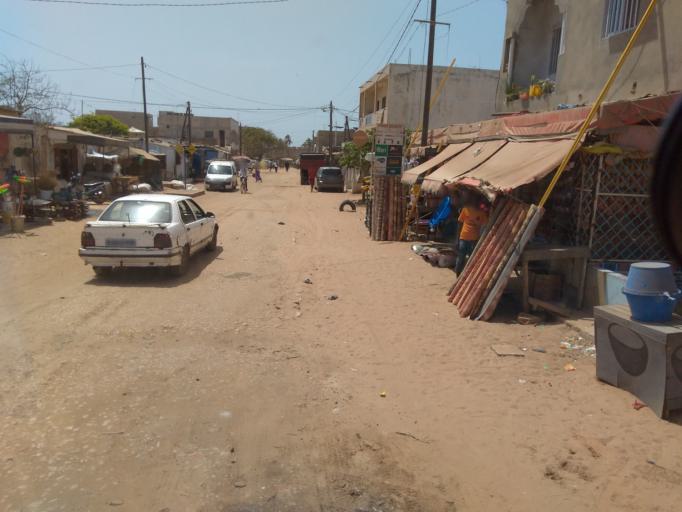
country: SN
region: Dakar
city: Pikine
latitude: 14.7888
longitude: -17.3395
